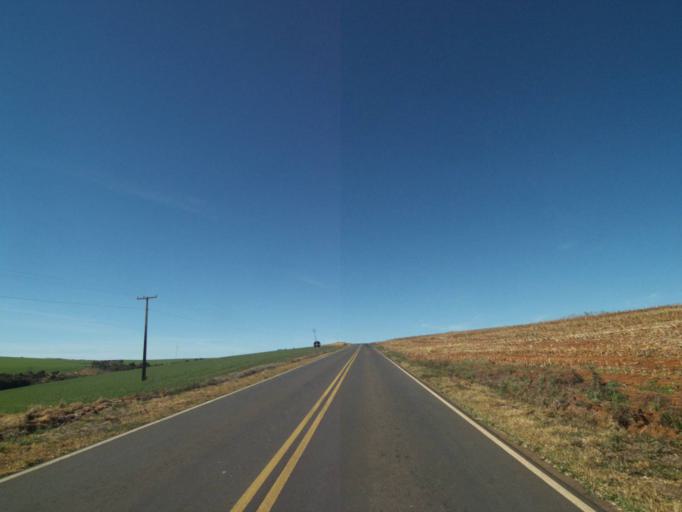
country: BR
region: Parana
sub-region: Tibagi
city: Tibagi
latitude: -24.5732
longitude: -50.2772
